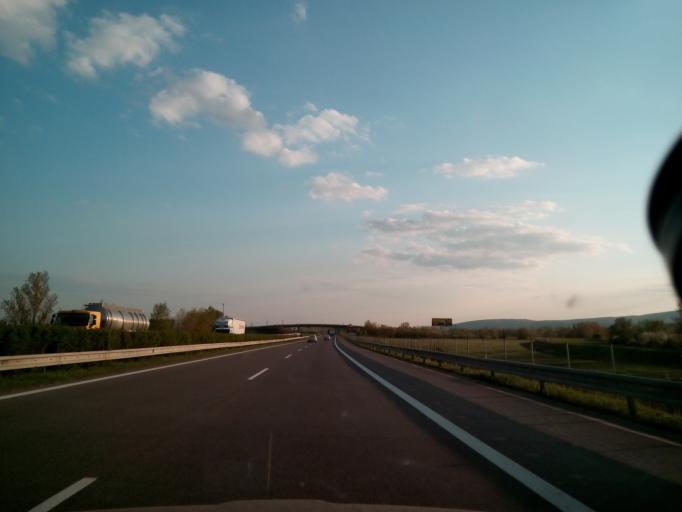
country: SK
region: Trenciansky
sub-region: Okres Nove Mesto nad Vahom
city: Nove Mesto nad Vahom
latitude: 48.7879
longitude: 17.8857
